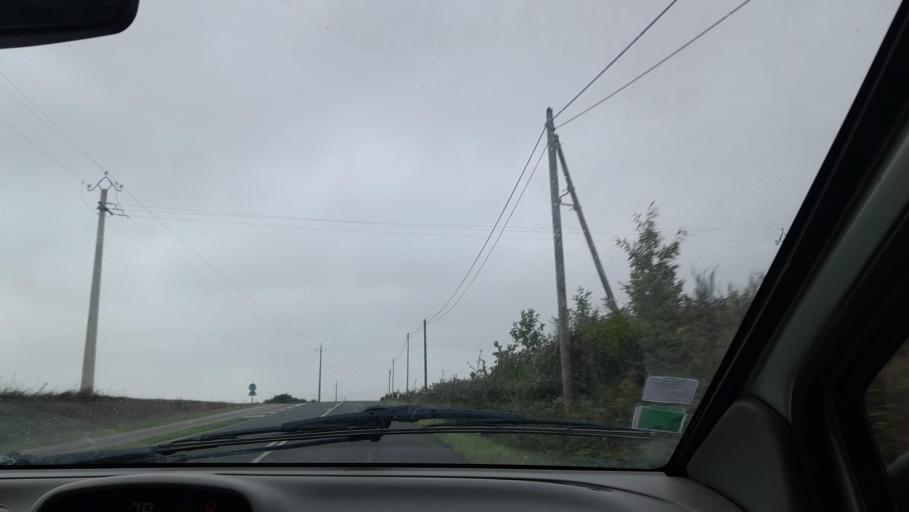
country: FR
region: Pays de la Loire
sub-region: Departement de Maine-et-Loire
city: Pouance
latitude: 47.7247
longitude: -1.1777
